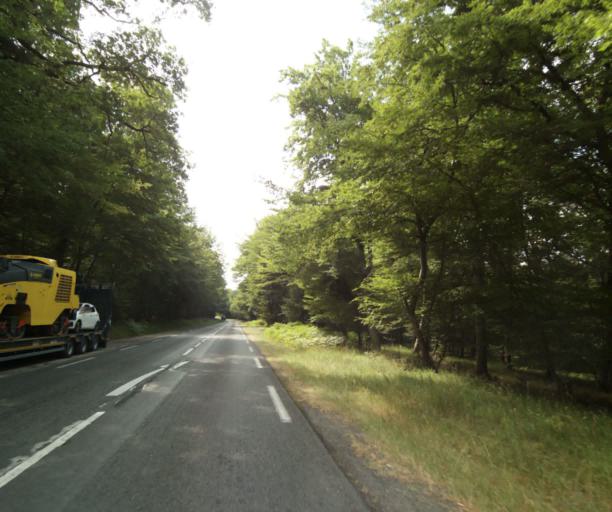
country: FR
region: Ile-de-France
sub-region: Departement de Seine-et-Marne
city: Fontainebleau
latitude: 48.4111
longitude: 2.6683
